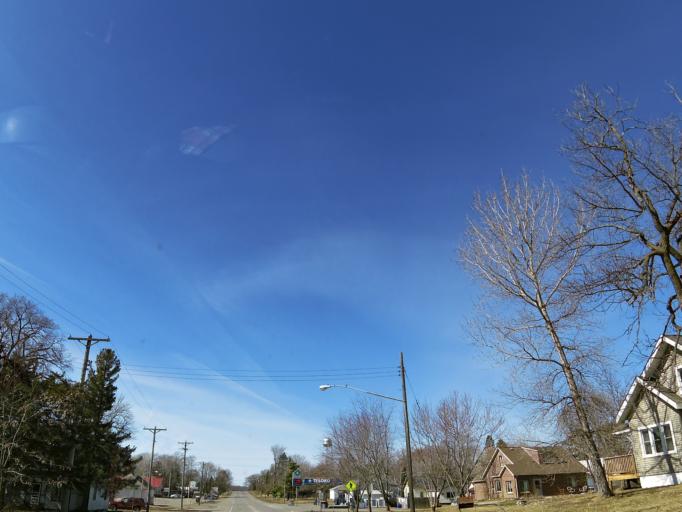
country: US
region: Minnesota
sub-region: Wright County
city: Annandale
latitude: 45.2928
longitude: -94.2131
